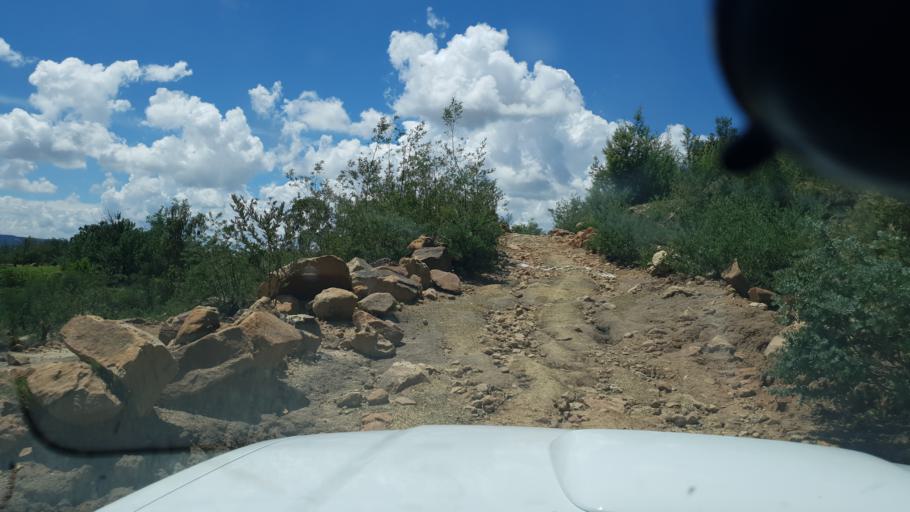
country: LS
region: Maseru
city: Nako
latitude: -29.6271
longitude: 27.5201
